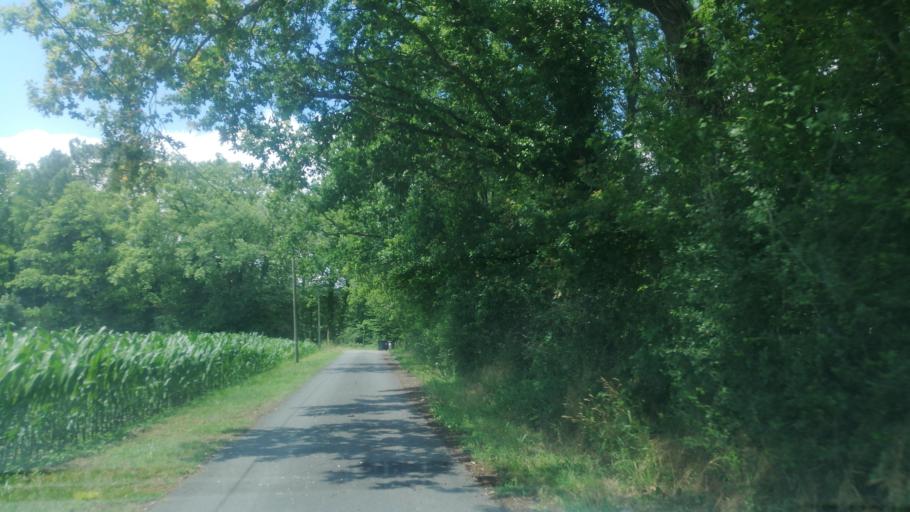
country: FR
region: Centre
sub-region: Departement du Loir-et-Cher
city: Contres
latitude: 47.3632
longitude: 1.4525
